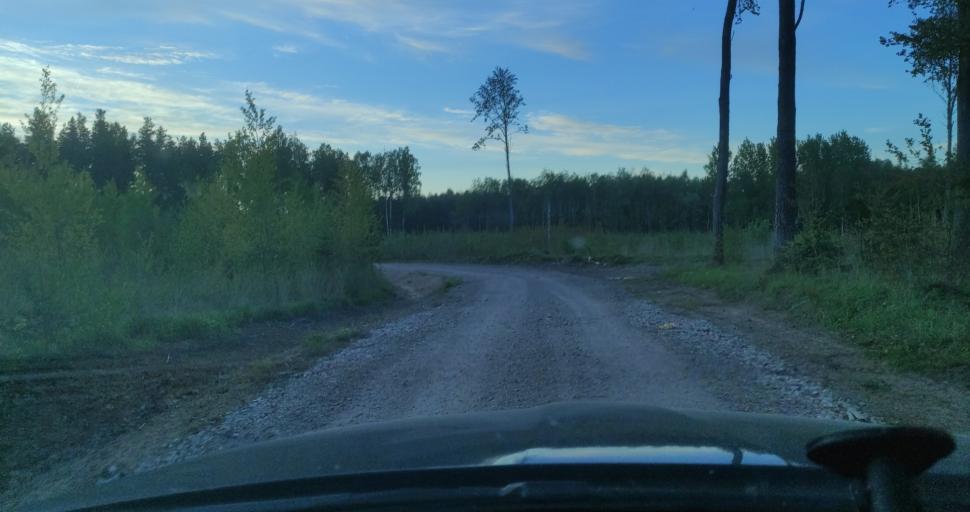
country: LV
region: Kuldigas Rajons
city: Kuldiga
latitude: 56.9493
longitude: 21.9161
